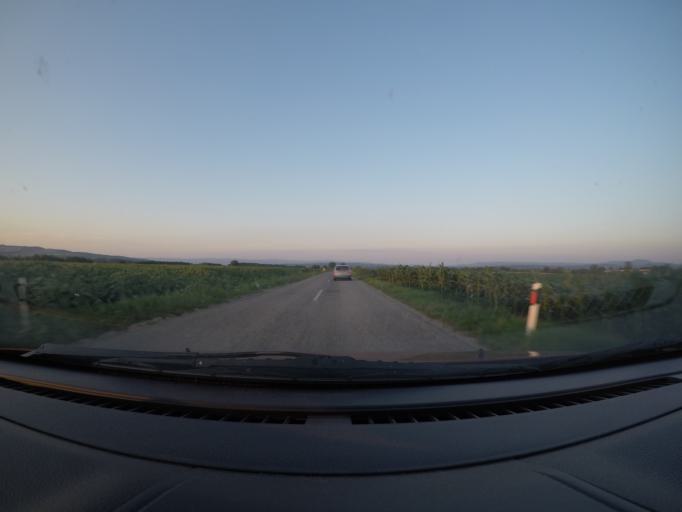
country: RS
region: Central Serbia
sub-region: Branicevski Okrug
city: Veliko Gradiste
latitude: 44.6473
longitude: 21.4619
